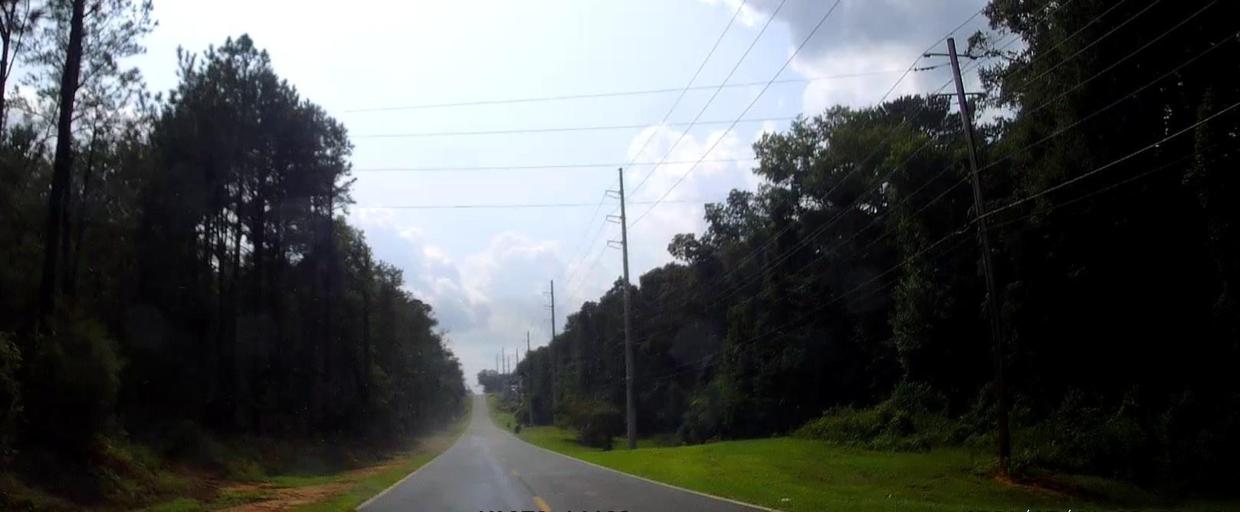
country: US
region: Georgia
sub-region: Houston County
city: Warner Robins
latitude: 32.6509
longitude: -83.6348
